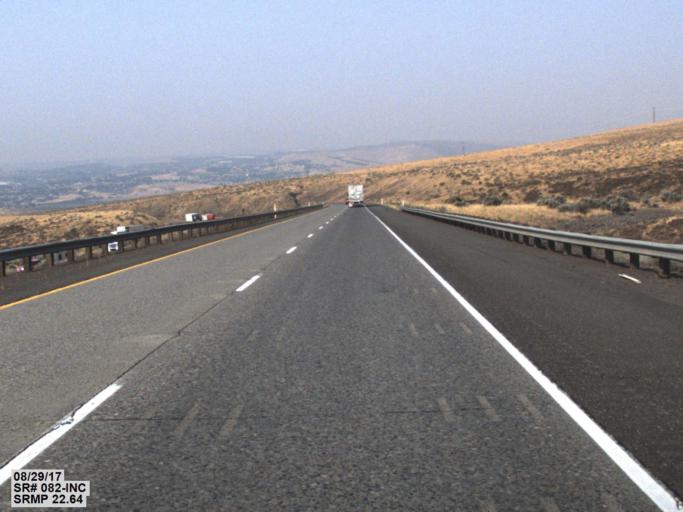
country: US
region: Washington
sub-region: Yakima County
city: Terrace Heights
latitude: 46.7134
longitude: -120.4219
